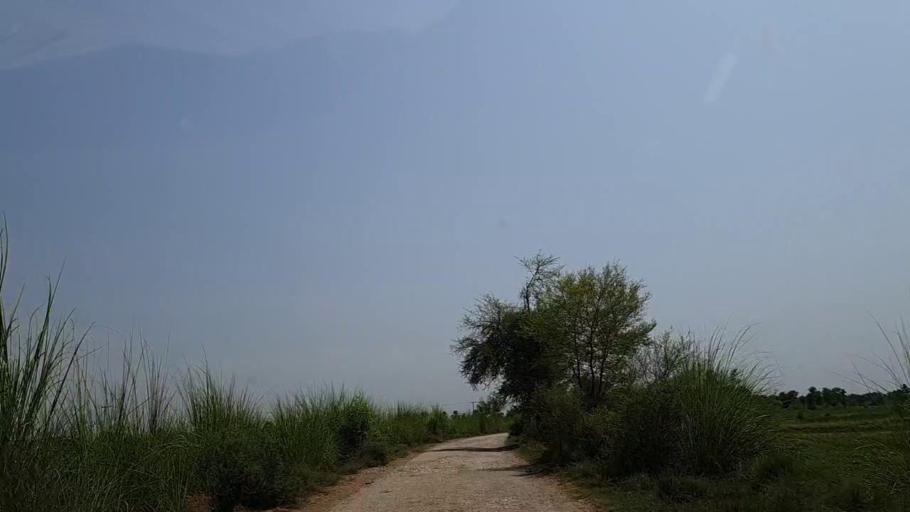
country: PK
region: Sindh
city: Adilpur
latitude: 27.9177
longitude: 69.3730
